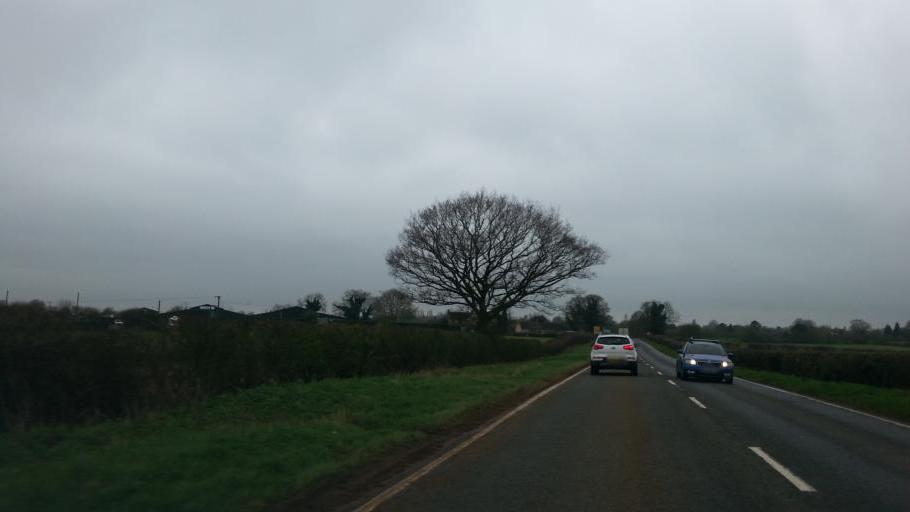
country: GB
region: England
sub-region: Oxfordshire
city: Adderbury
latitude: 52.0659
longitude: -1.2546
